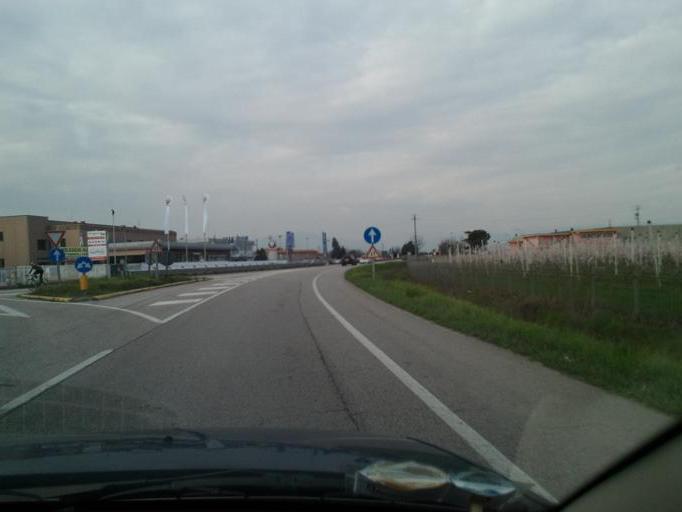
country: IT
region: Veneto
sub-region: Provincia di Verona
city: Sona
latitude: 45.4326
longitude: 10.8478
